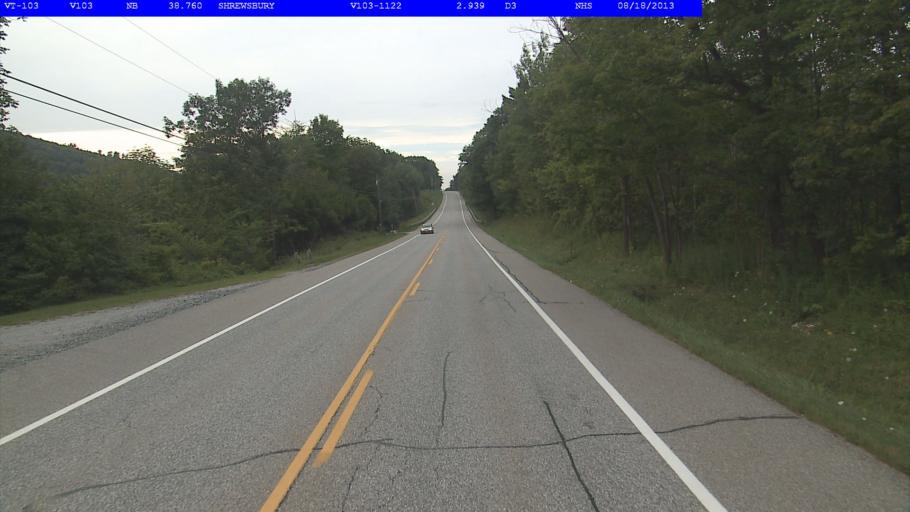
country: US
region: Vermont
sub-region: Rutland County
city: Rutland
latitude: 43.5114
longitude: -72.9124
